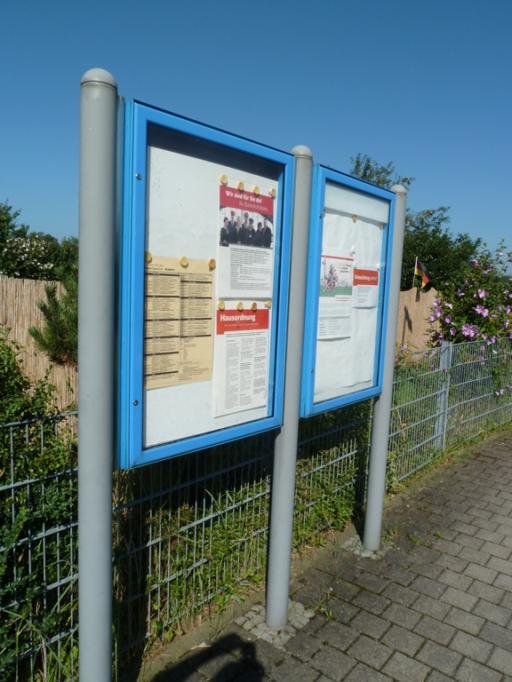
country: DE
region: Baden-Wuerttemberg
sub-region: Tuebingen Region
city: Eriskirch
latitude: 47.6271
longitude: 9.5278
